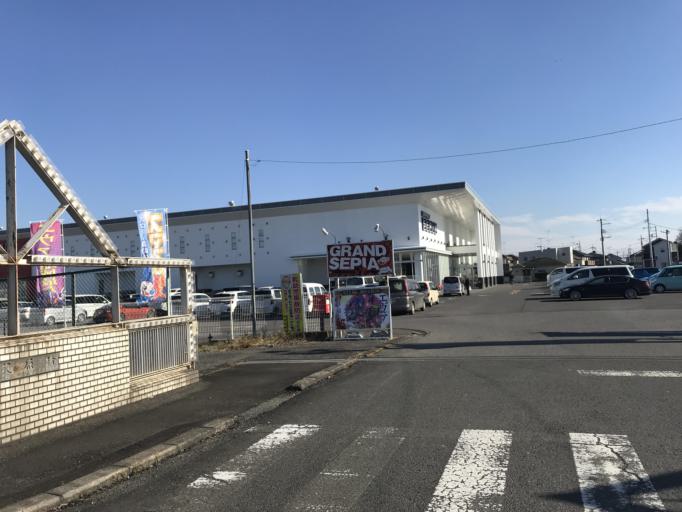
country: JP
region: Ibaraki
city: Yuki
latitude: 36.2924
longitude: 139.8635
